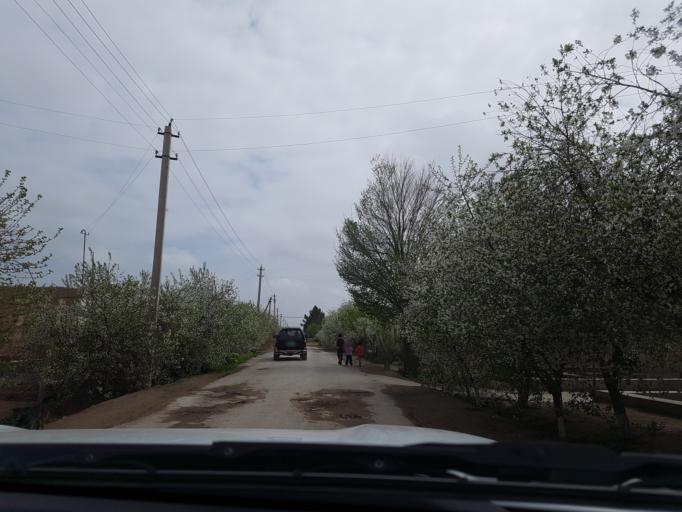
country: TM
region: Lebap
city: Turkmenabat
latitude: 38.9714
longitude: 63.6916
